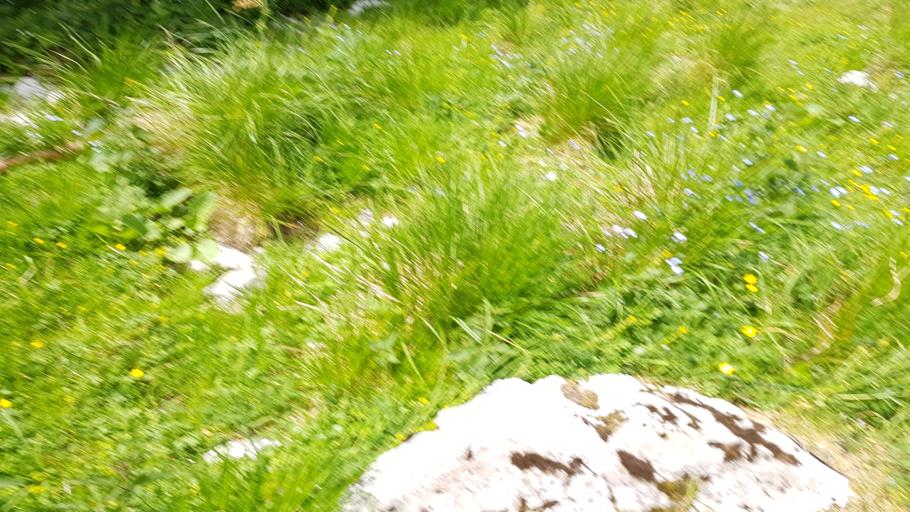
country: IT
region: Friuli Venezia Giulia
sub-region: Provincia di Udine
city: Paularo
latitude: 46.5302
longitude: 13.1815
